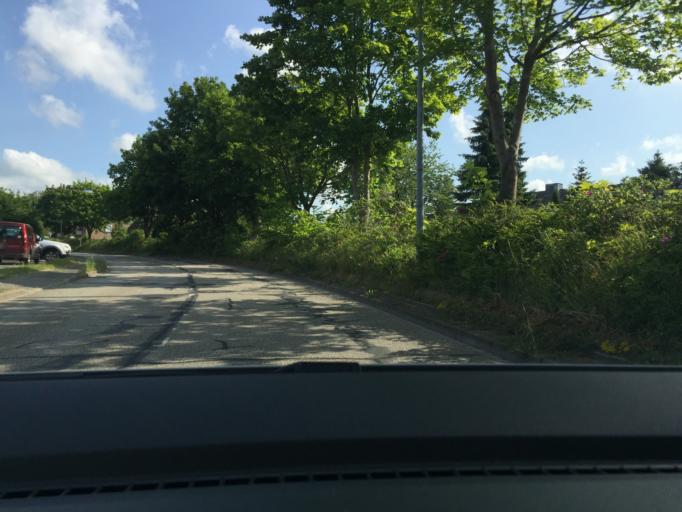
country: DE
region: Schleswig-Holstein
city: Itzehoe
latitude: 53.9441
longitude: 9.5063
